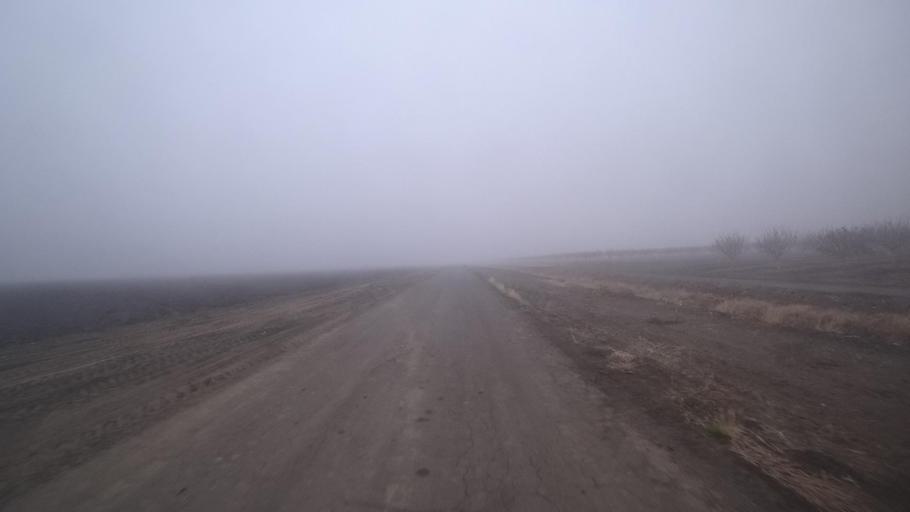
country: US
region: California
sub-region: Kern County
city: Buttonwillow
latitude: 35.4562
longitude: -119.5568
